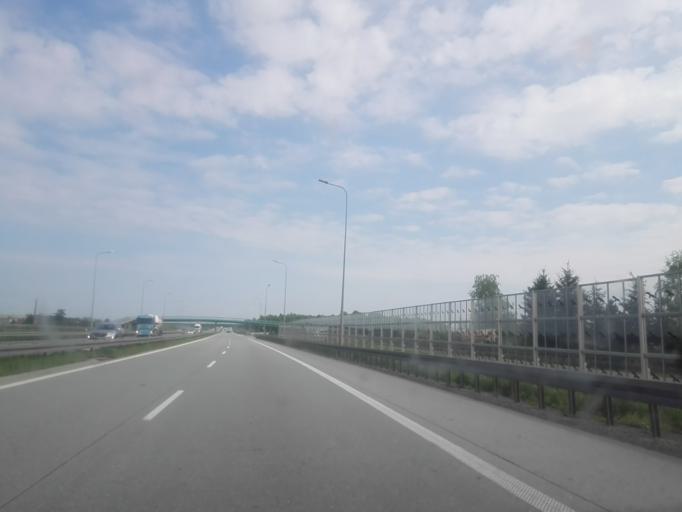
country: PL
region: Lodz Voivodeship
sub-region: Powiat skierniewicki
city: Kowiesy
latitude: 51.8643
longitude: 20.3833
